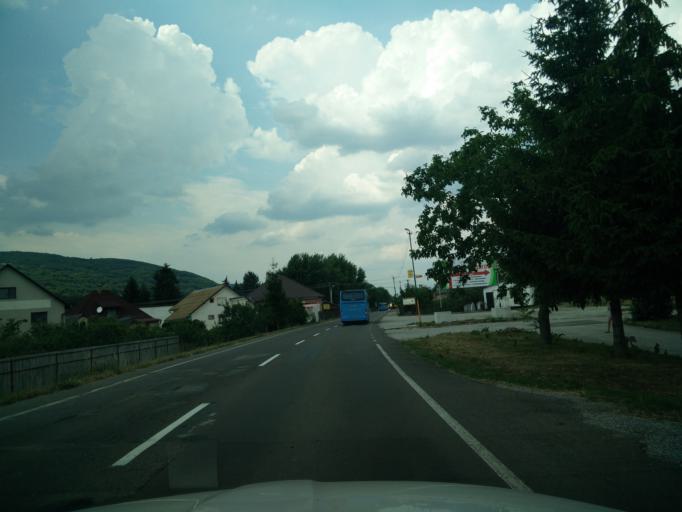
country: SK
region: Nitriansky
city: Novaky
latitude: 48.7480
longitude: 18.4977
